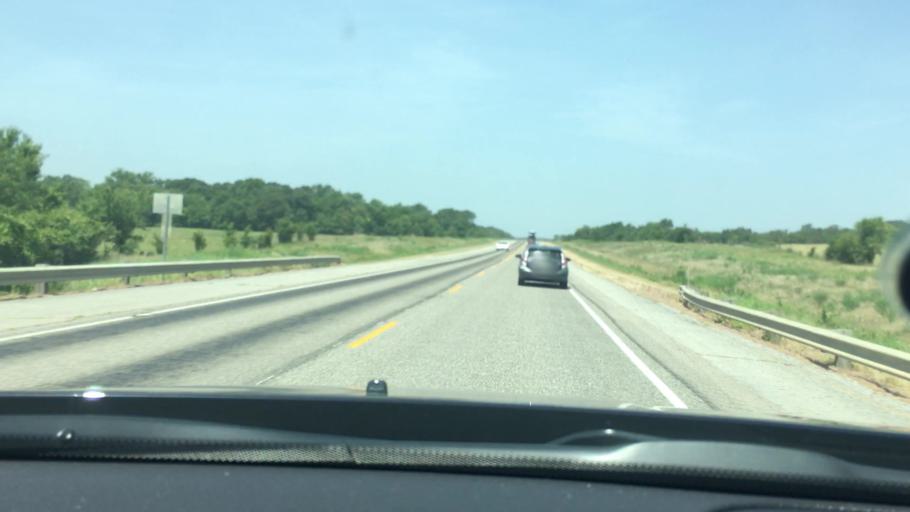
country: US
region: Oklahoma
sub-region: Coal County
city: Coalgate
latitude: 34.6002
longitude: -96.3367
